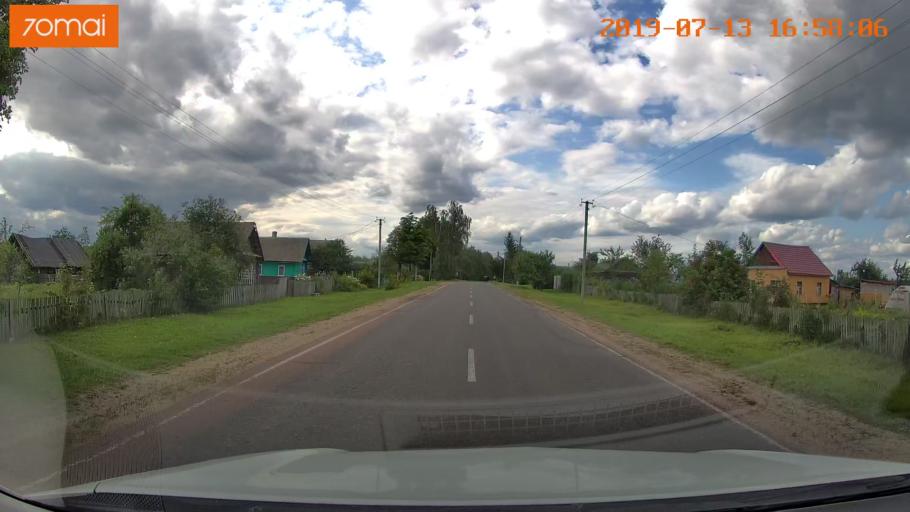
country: BY
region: Mogilev
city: Kirawsk
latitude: 53.2853
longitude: 29.4452
